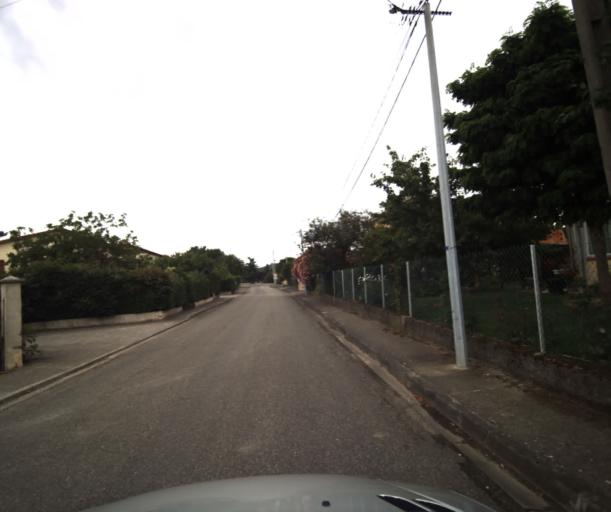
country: FR
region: Midi-Pyrenees
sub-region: Departement de la Haute-Garonne
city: Labarthe-sur-Leze
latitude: 43.4562
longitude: 1.4037
